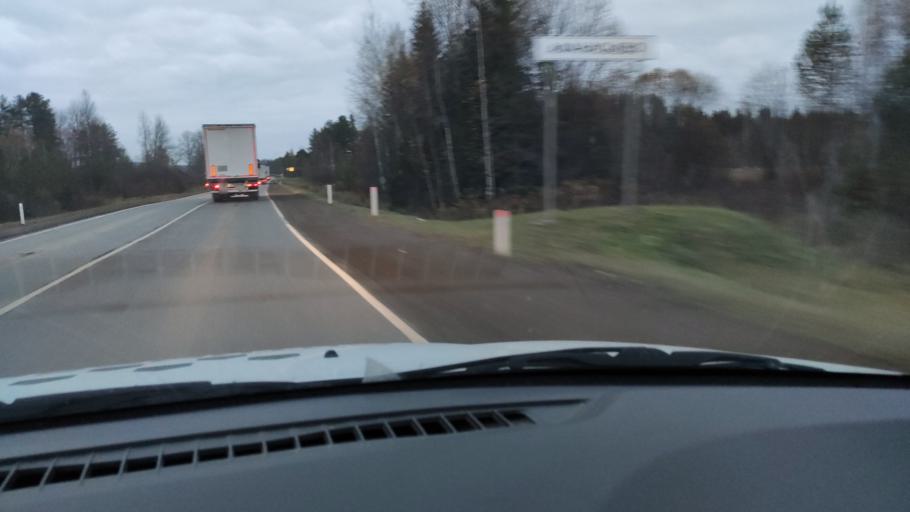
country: RU
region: Kirov
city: Kostino
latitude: 58.8541
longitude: 53.2126
